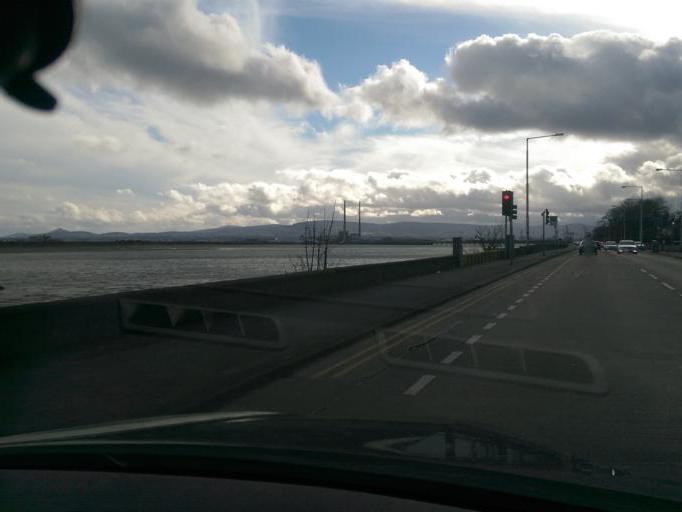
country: IE
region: Leinster
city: Dollymount
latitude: 53.3674
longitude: -6.1722
